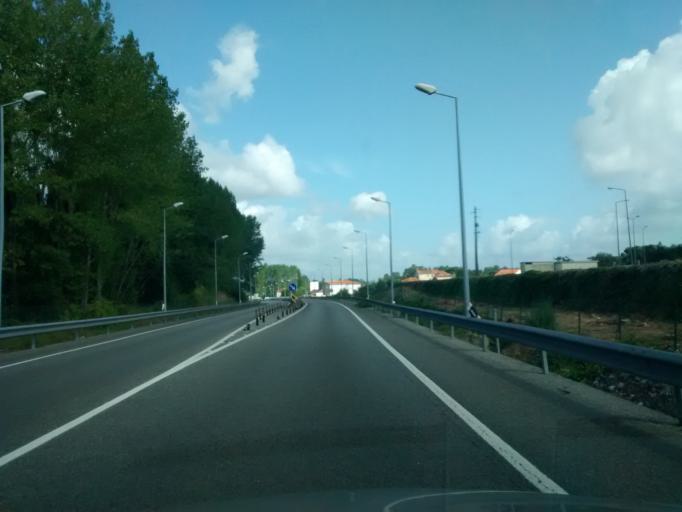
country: PT
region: Aveiro
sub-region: Anadia
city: Sangalhos
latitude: 40.4789
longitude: -8.4769
